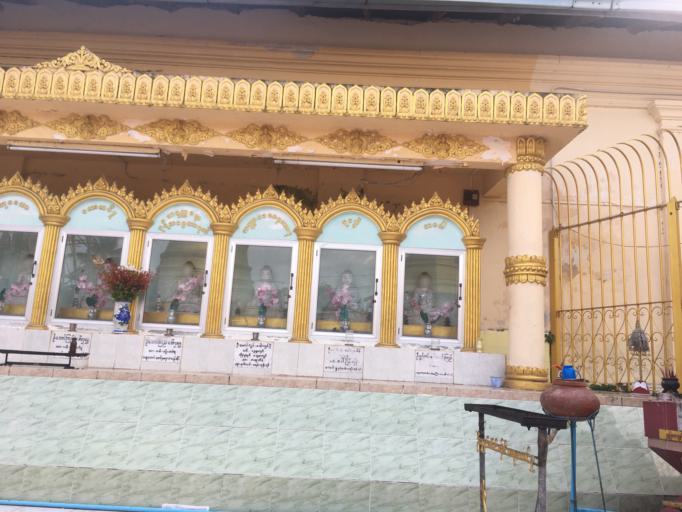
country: MM
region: Mon
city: Mawlamyine
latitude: 16.4792
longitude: 97.6220
